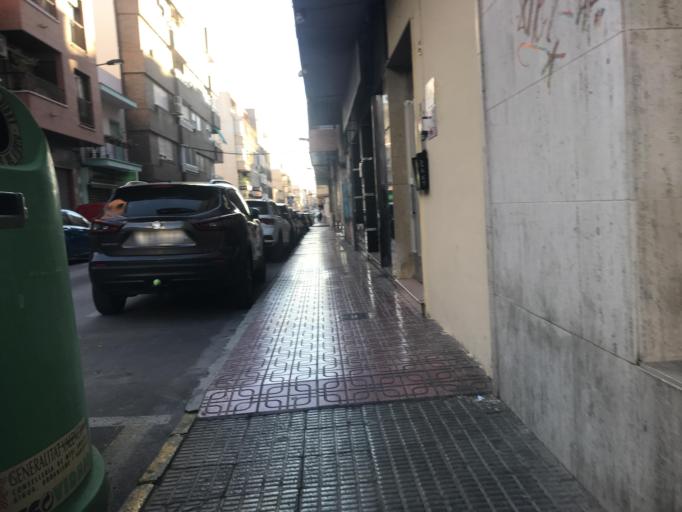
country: ES
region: Valencia
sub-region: Provincia de Alicante
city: Torrevieja
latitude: 37.9784
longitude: -0.6832
